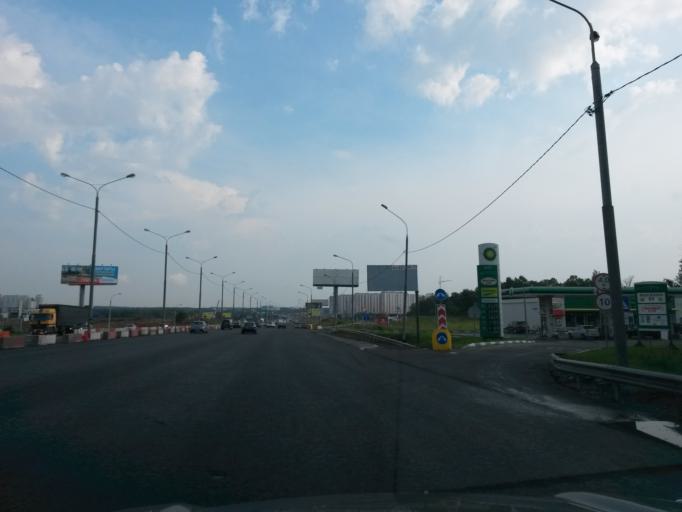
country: RU
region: Moskovskaya
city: Shcherbinka
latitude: 55.5196
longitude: 37.6090
